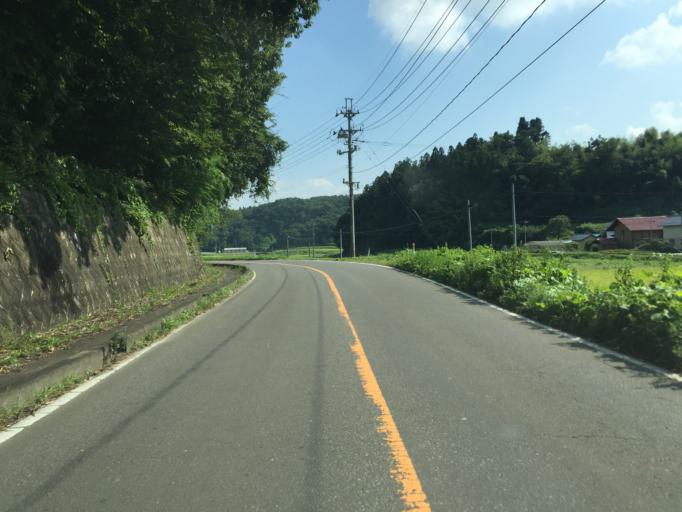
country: JP
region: Fukushima
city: Nihommatsu
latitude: 37.5917
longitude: 140.4091
